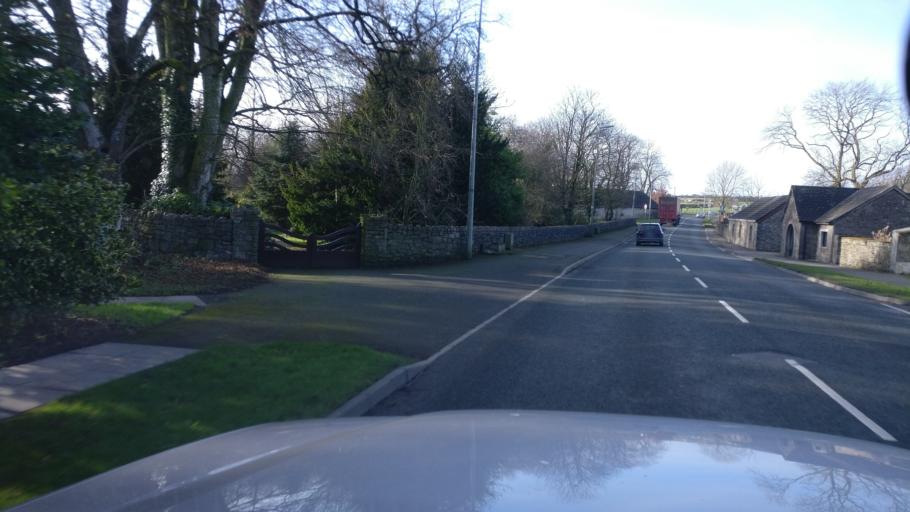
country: IE
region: Leinster
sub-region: Uibh Fhaili
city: Tullamore
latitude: 53.2143
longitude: -7.4517
